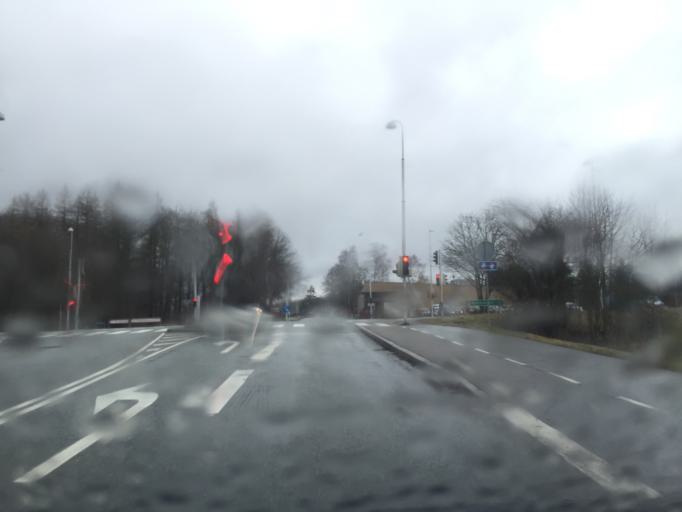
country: DK
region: Capital Region
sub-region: Fureso Kommune
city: Farum
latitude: 55.8212
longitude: 12.3390
